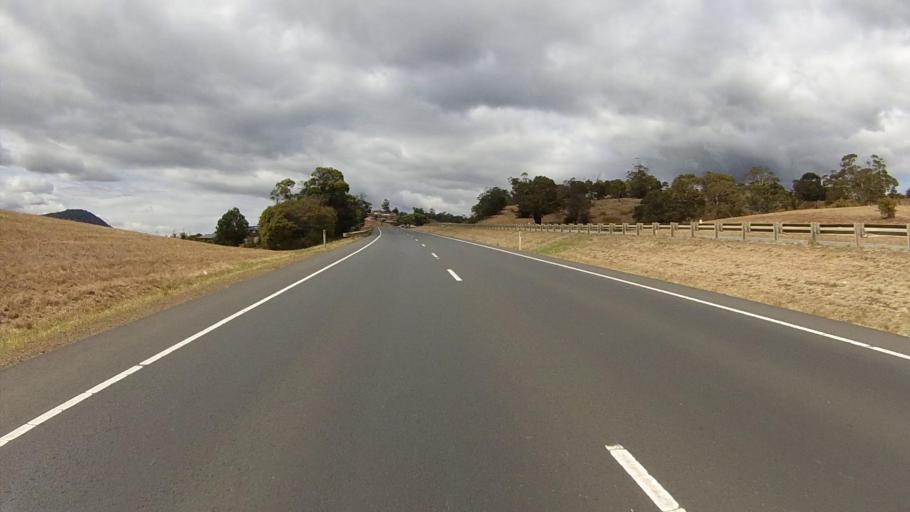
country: AU
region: Tasmania
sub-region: Glenorchy
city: Austins Ferry
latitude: -42.7688
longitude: 147.2367
